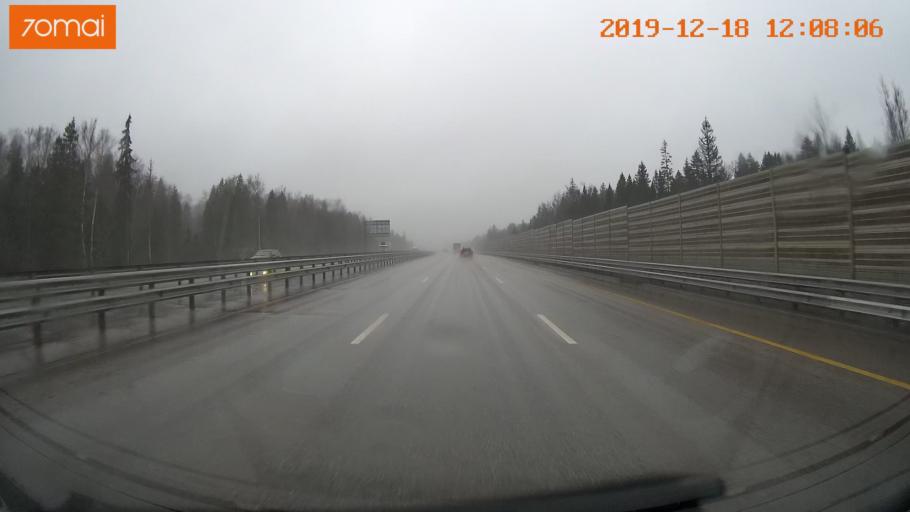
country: RU
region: Moskovskaya
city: Kostrovo
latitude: 55.8968
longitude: 36.6424
